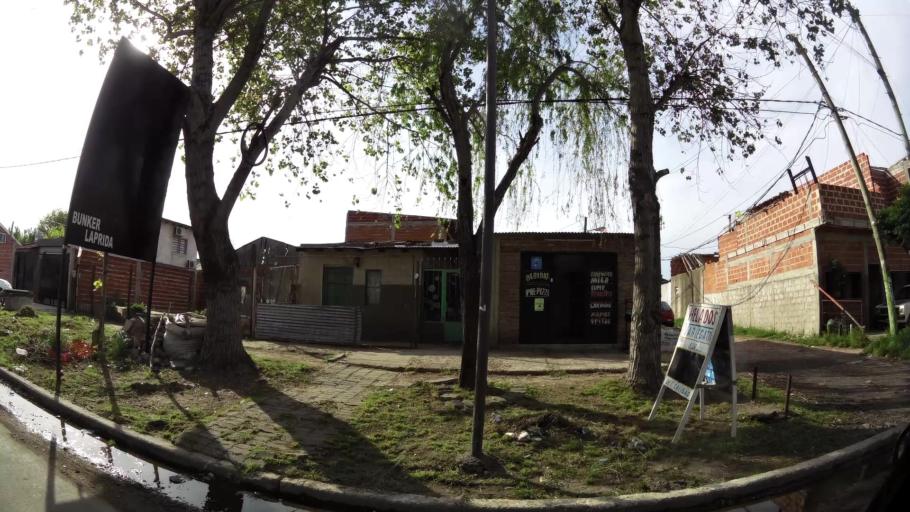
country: AR
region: Buenos Aires
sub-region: Partido de Quilmes
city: Quilmes
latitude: -34.7446
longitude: -58.2642
